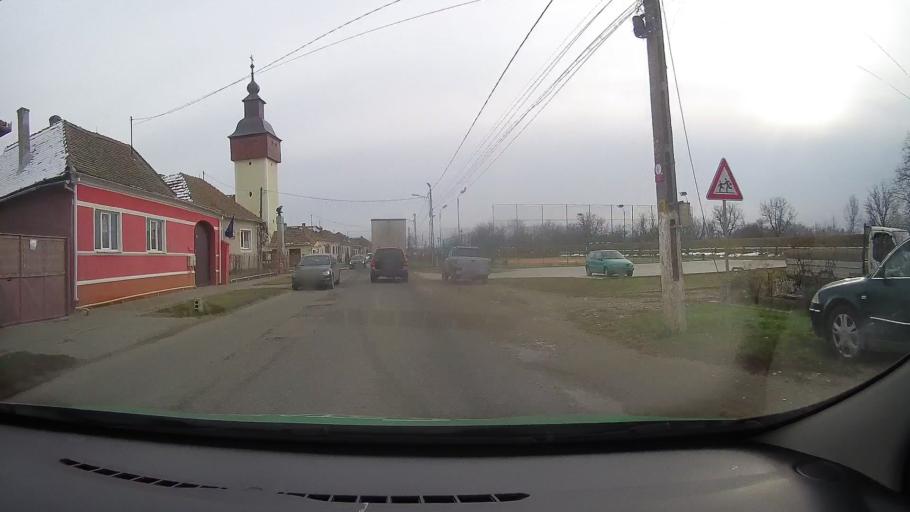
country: RO
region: Hunedoara
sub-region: Comuna Geoagiu
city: Geoagiu
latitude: 45.9015
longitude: 23.2237
